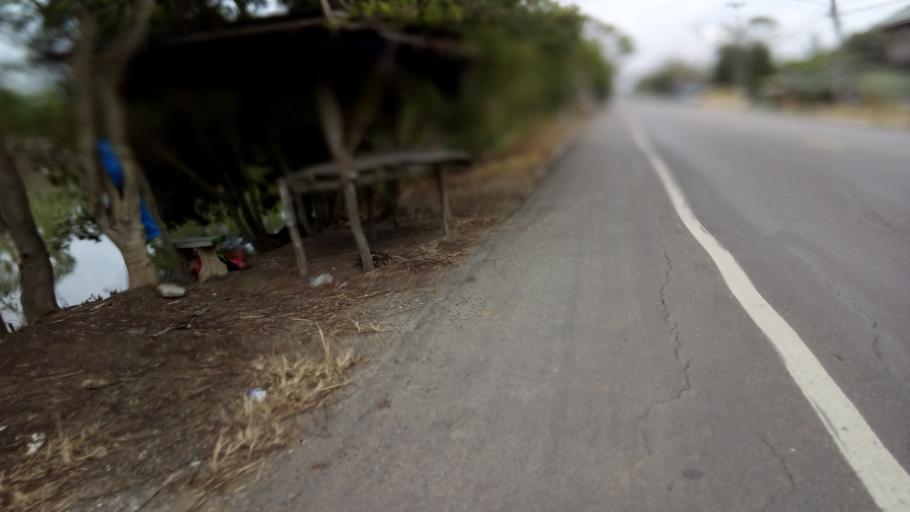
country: TH
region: Pathum Thani
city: Nong Suea
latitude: 14.2069
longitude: 100.8234
